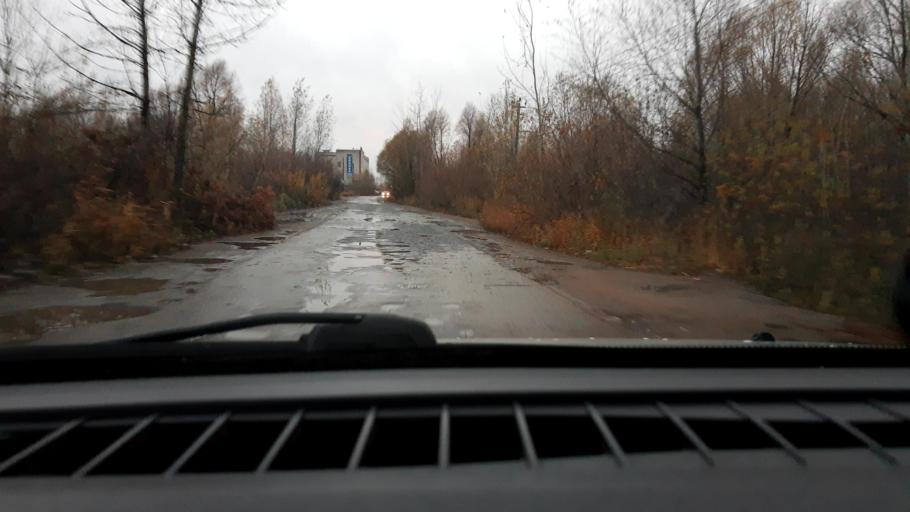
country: RU
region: Nizjnij Novgorod
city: Gorbatovka
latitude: 56.2685
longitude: 43.8564
